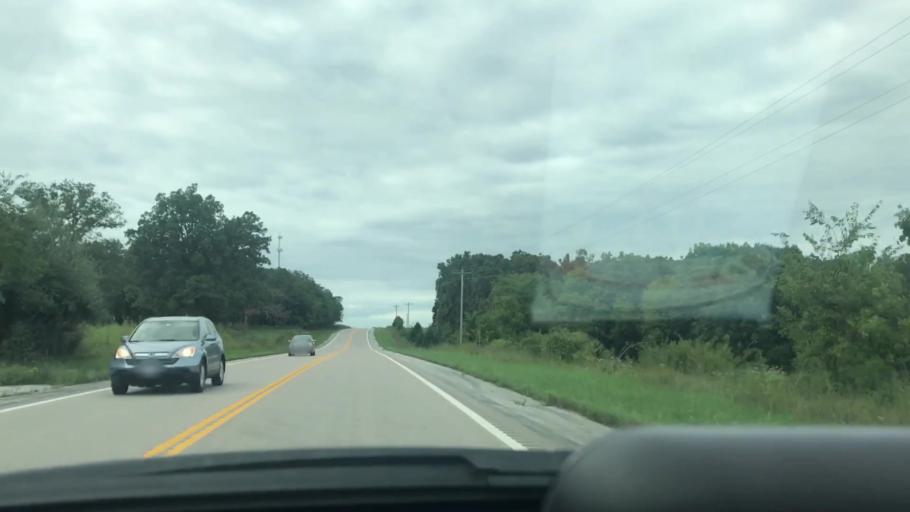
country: US
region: Missouri
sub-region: Benton County
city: Warsaw
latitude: 38.1411
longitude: -93.2872
